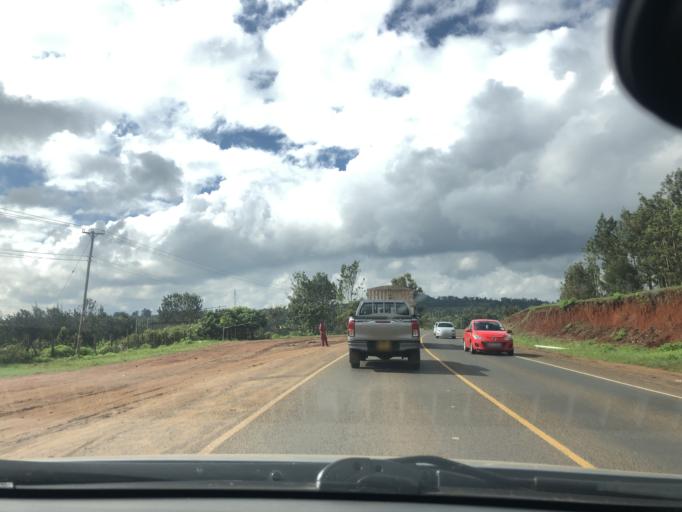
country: KE
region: Murang'a District
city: Maragua
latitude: -0.8654
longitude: 37.2387
